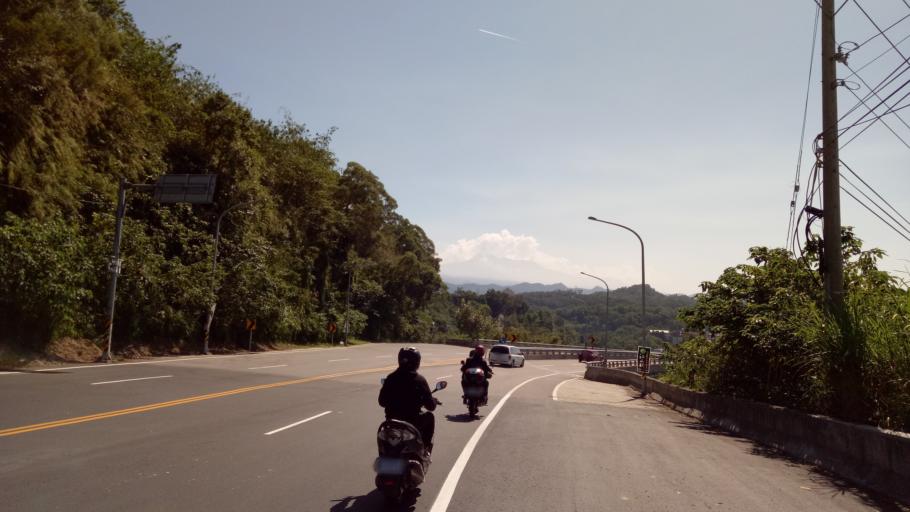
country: TW
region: Taiwan
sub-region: Hsinchu
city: Hsinchu
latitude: 24.6734
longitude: 120.9661
